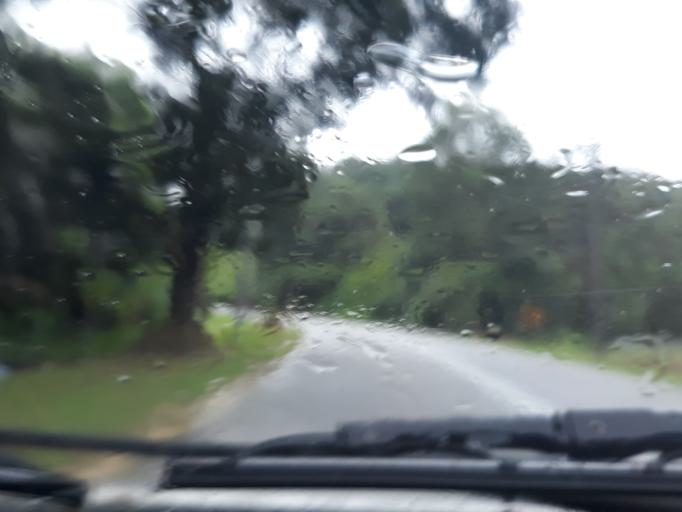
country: MY
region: Kedah
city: Kulim
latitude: 5.2801
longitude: 100.6216
